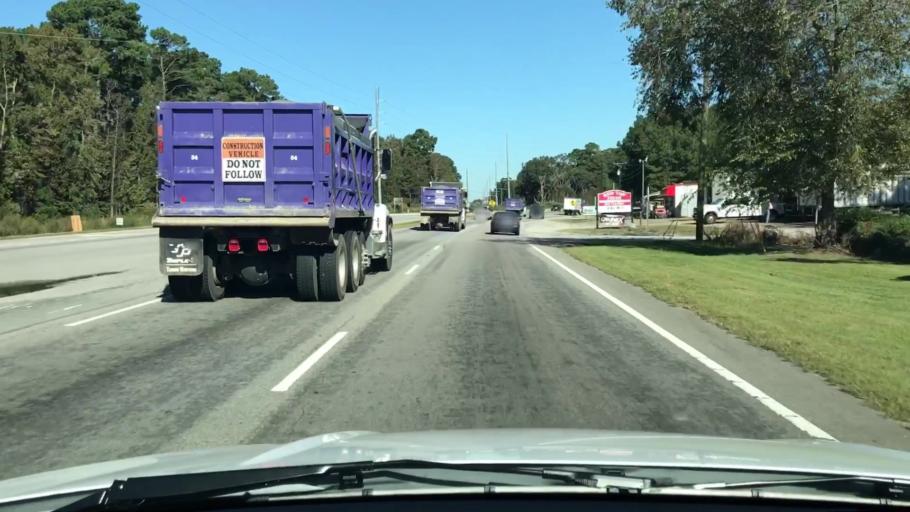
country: US
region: South Carolina
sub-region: Charleston County
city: Shell Point
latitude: 32.8023
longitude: -80.1230
